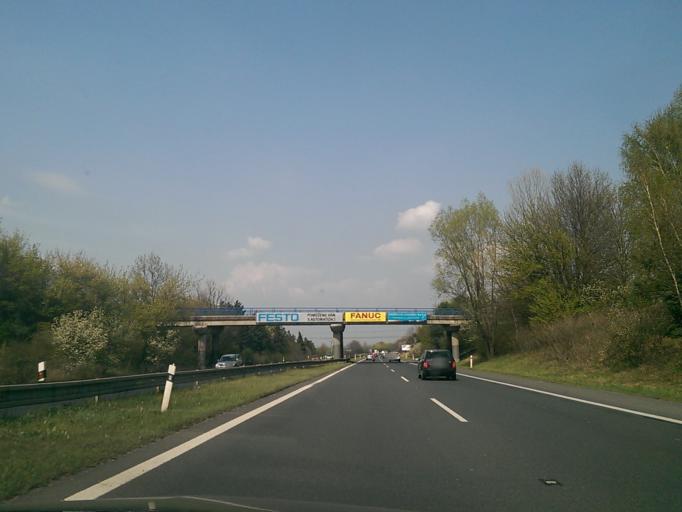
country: CZ
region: Central Bohemia
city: Zelenec
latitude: 50.1571
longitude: 14.6621
